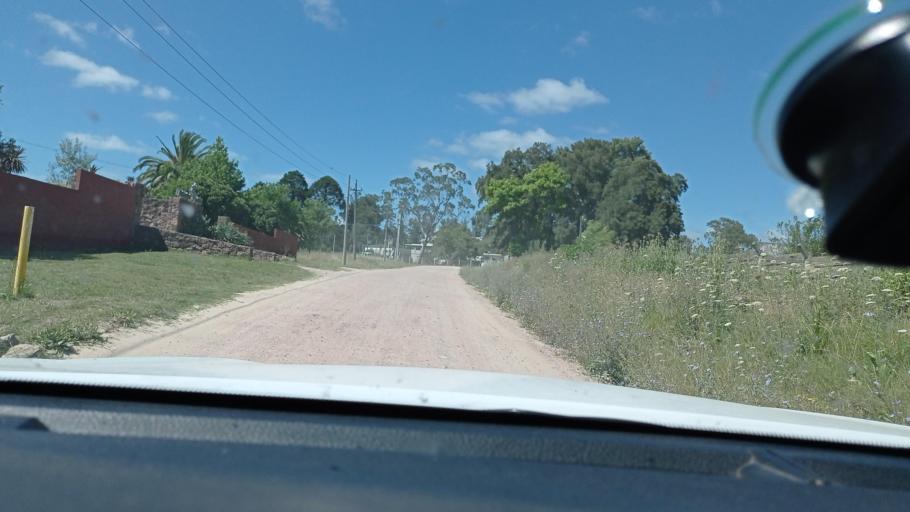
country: UY
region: Canelones
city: Pando
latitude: -34.7321
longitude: -55.9758
